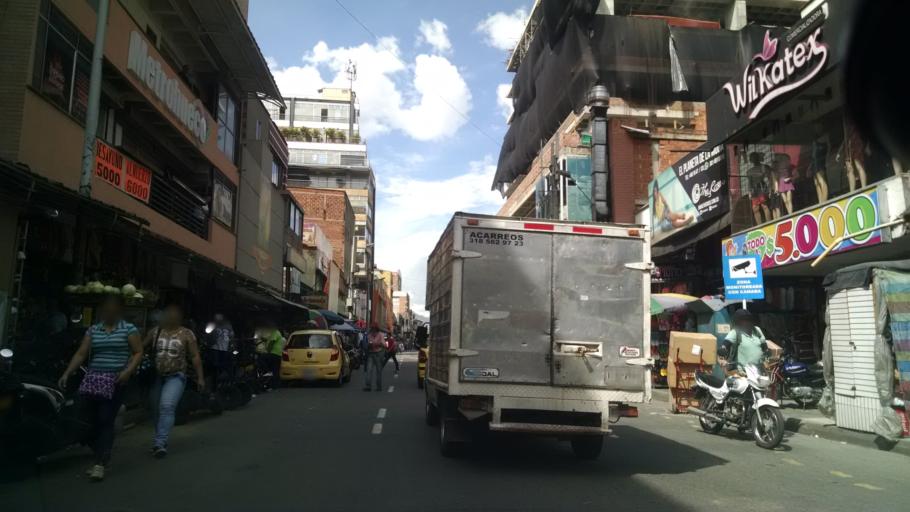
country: CO
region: Antioquia
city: Medellin
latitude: 6.2481
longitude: -75.5714
